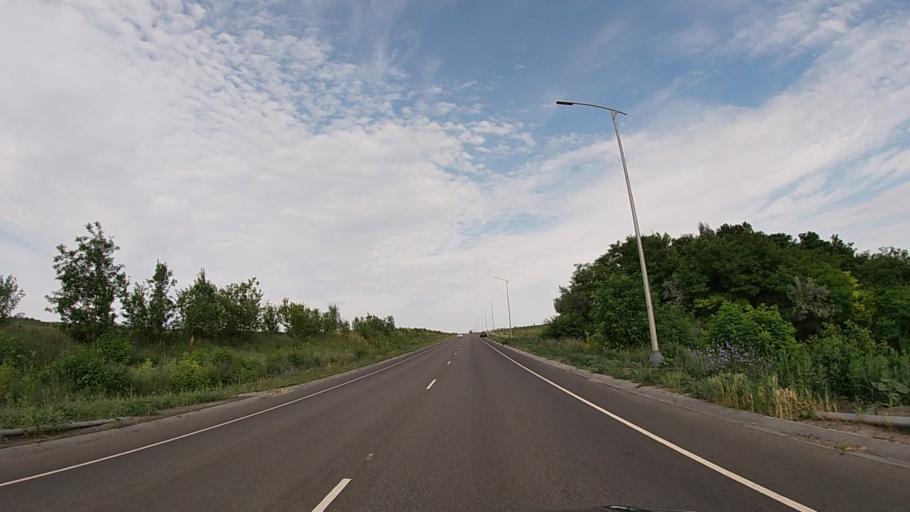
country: RU
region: Belgorod
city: Severnyy
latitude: 50.6645
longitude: 36.5183
